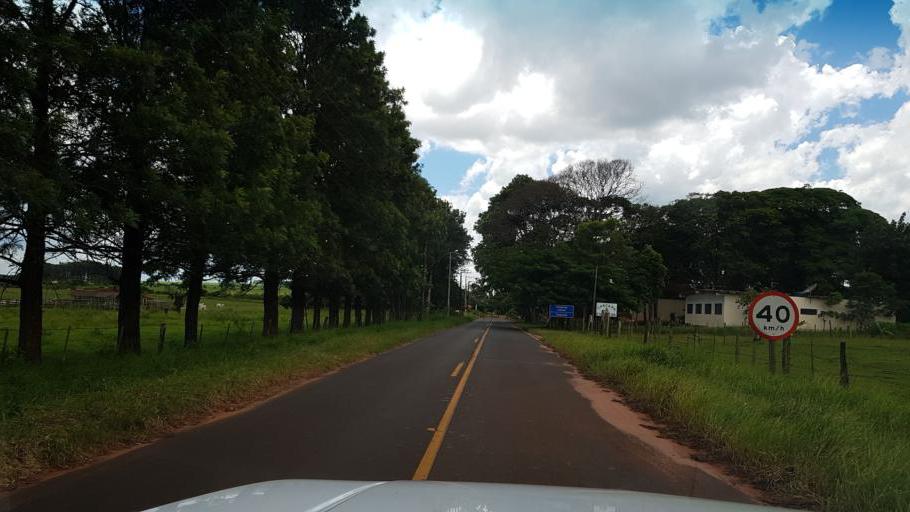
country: BR
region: Sao Paulo
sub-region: Paraguacu Paulista
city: Paraguacu Paulista
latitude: -22.3540
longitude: -50.6247
